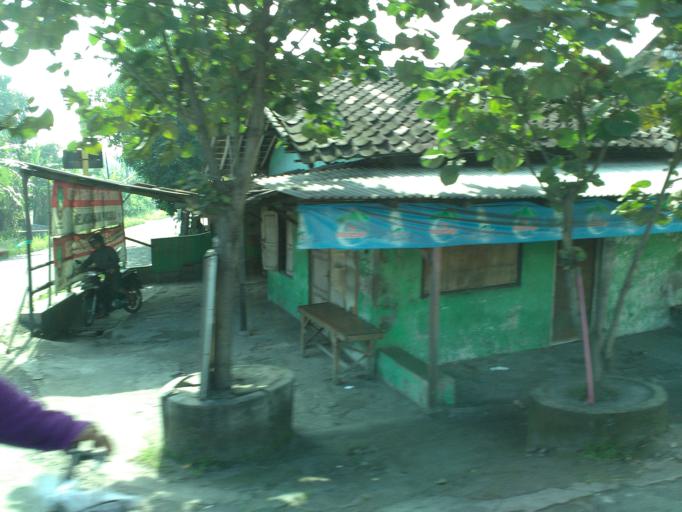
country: ID
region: Central Java
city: Delanggu
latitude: -7.6312
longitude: 110.6940
